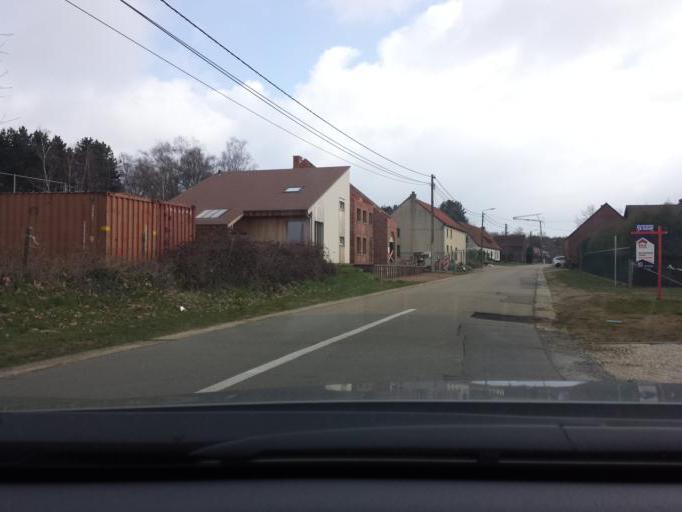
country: BE
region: Flanders
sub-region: Provincie Limburg
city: Halen
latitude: 50.9670
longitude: 5.1408
